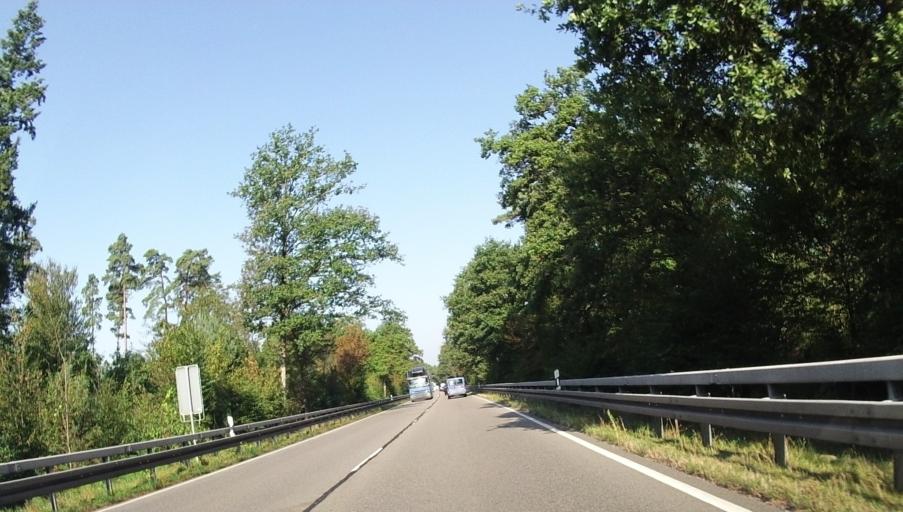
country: DE
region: Baden-Wuerttemberg
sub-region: Karlsruhe Region
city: Iffezheim
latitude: 48.7988
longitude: 8.1517
